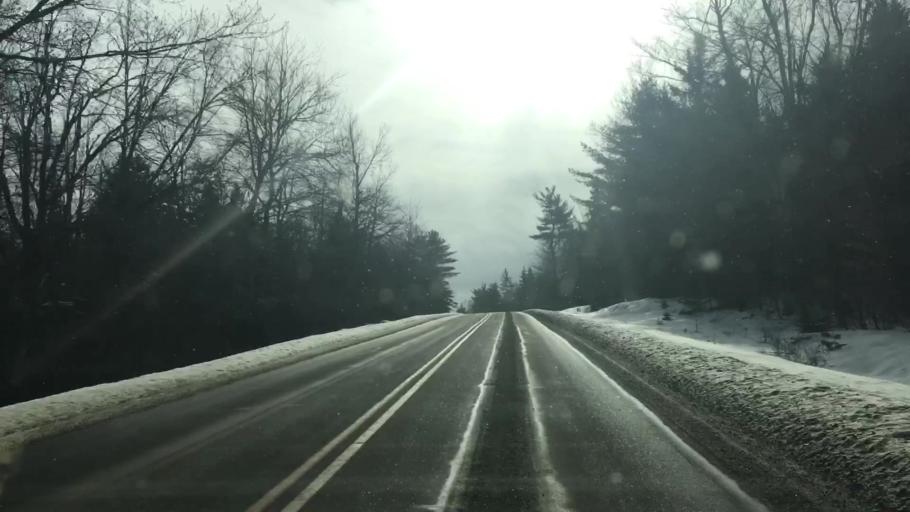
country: US
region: Maine
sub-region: Washington County
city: Calais
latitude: 45.0666
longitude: -67.3304
